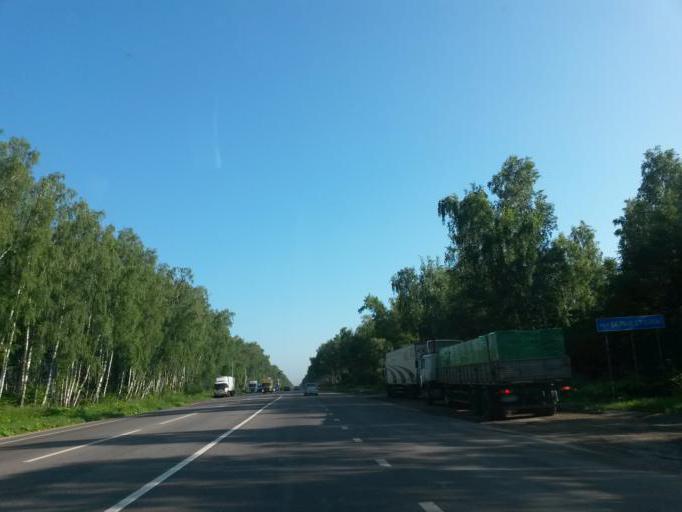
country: RU
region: Moskovskaya
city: Belyye Stolby
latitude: 55.2779
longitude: 37.8248
